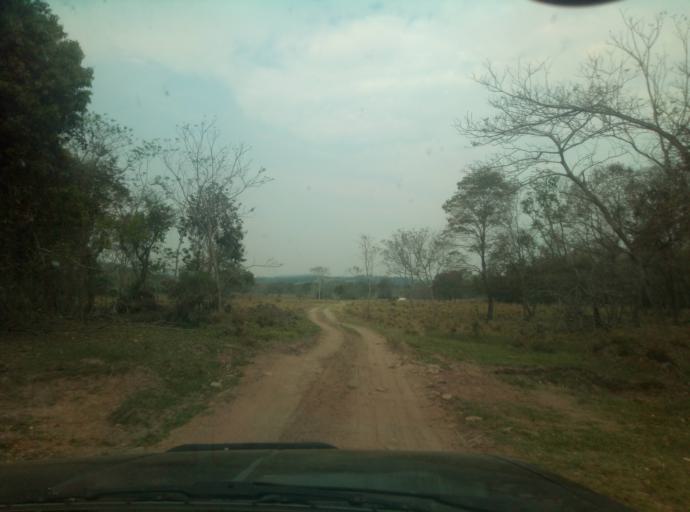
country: PY
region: Caaguazu
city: San Joaquin
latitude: -25.1033
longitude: -56.1210
